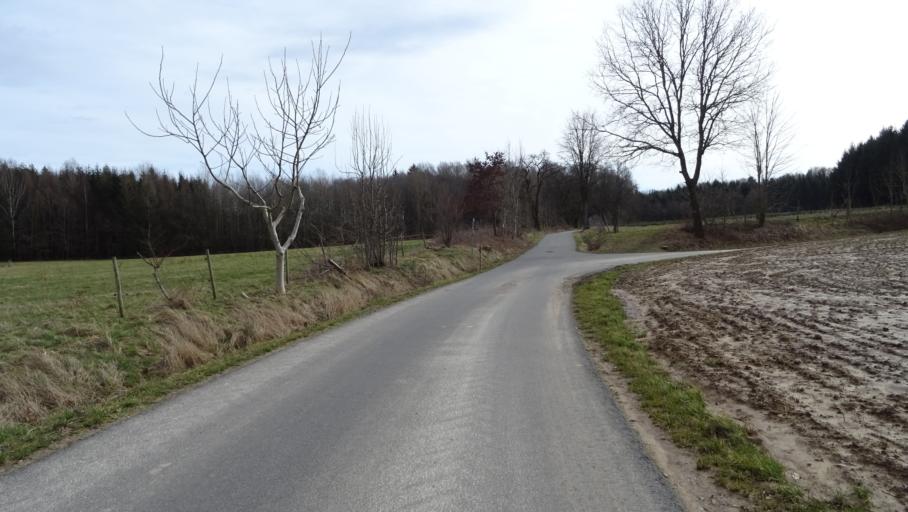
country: DE
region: Baden-Wuerttemberg
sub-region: Karlsruhe Region
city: Limbach
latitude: 49.4490
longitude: 9.2542
